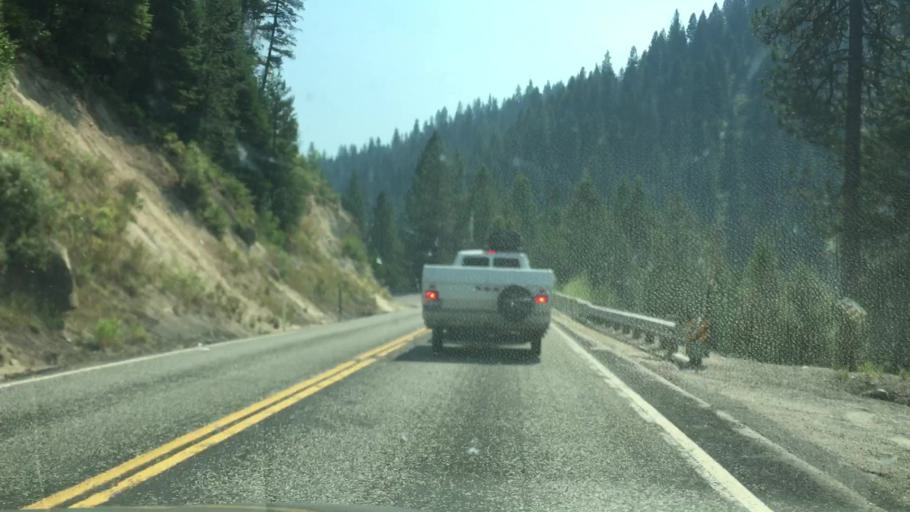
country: US
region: Idaho
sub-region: Valley County
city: Cascade
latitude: 44.3295
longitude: -116.0577
